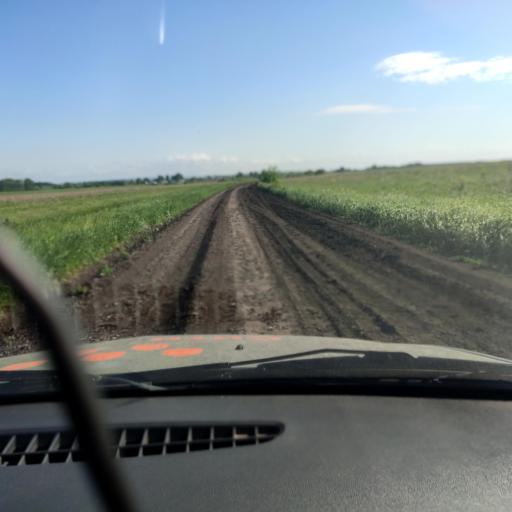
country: RU
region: Bashkortostan
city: Avdon
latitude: 54.5665
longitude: 55.8315
